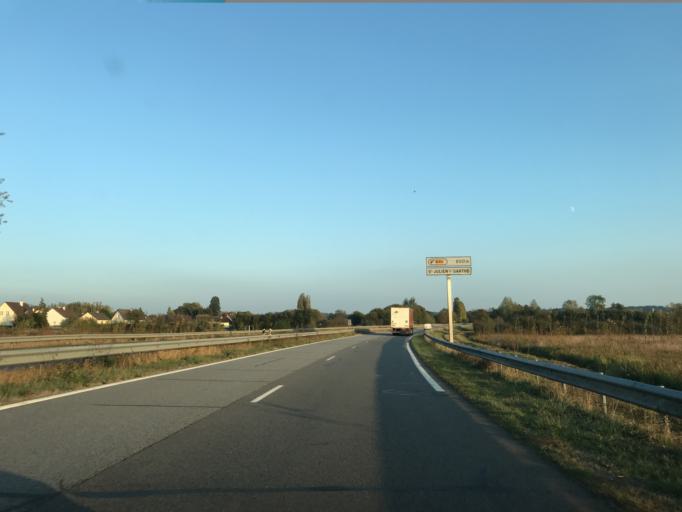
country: FR
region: Pays de la Loire
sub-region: Departement de la Sarthe
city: Mamers
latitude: 48.5093
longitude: 0.3501
